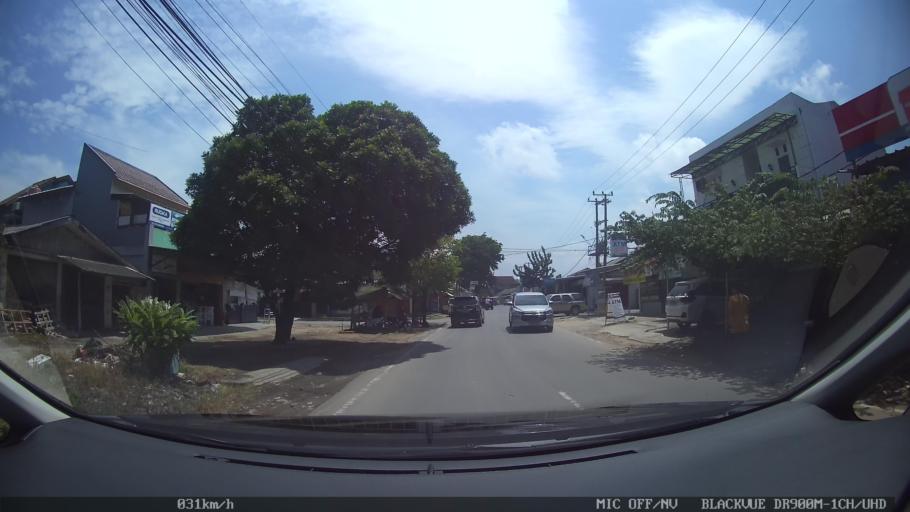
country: ID
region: Lampung
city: Kedaton
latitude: -5.3625
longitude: 105.2895
